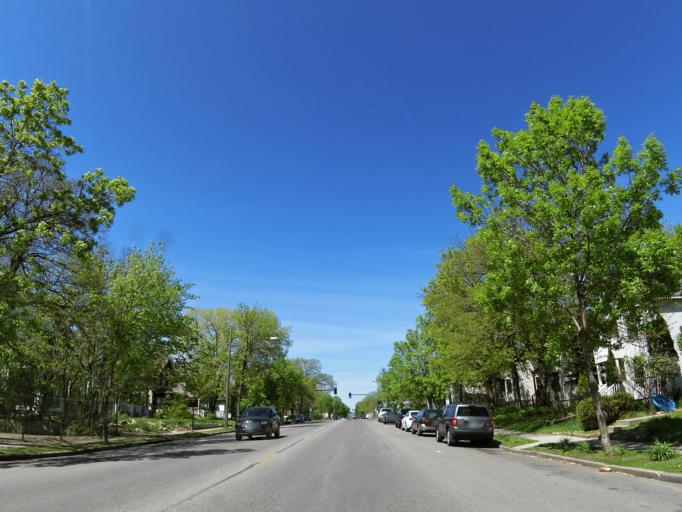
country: US
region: Minnesota
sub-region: Hennepin County
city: Minneapolis
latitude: 44.9366
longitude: -93.2625
